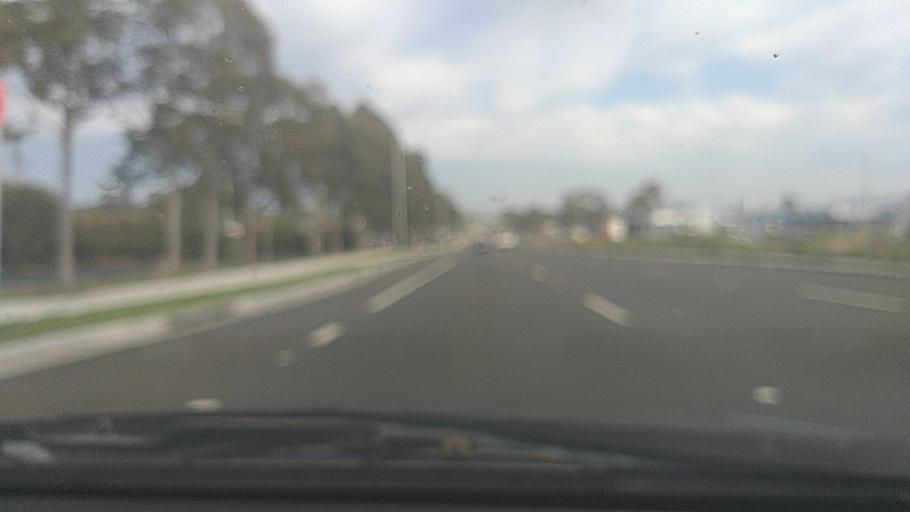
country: AU
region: New South Wales
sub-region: Camden
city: Narellan Vale
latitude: -34.0430
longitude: 150.7531
